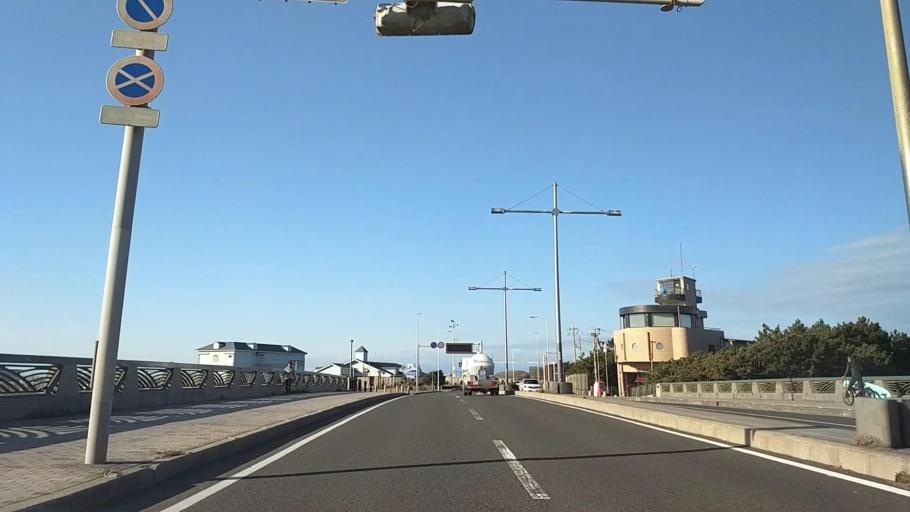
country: JP
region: Kanagawa
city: Fujisawa
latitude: 35.3172
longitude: 139.4677
